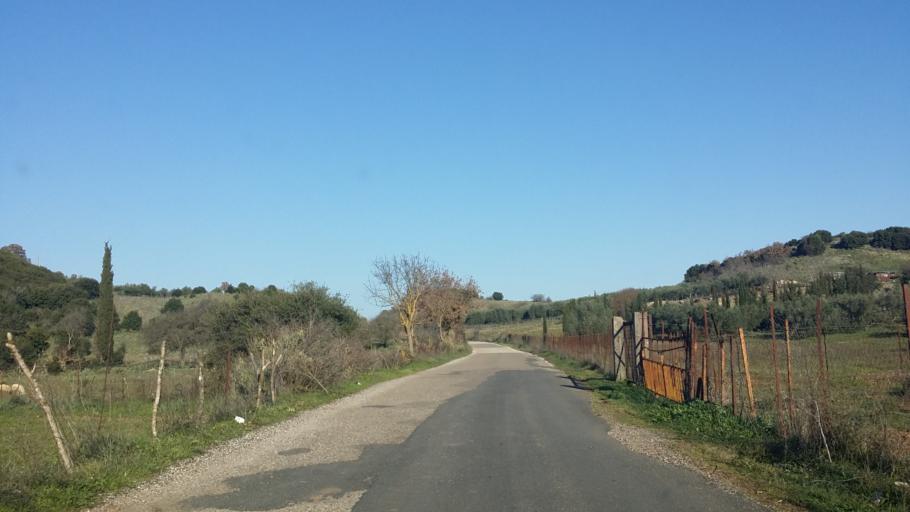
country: GR
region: West Greece
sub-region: Nomos Aitolias kai Akarnanias
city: Katouna
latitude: 38.7913
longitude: 21.1054
